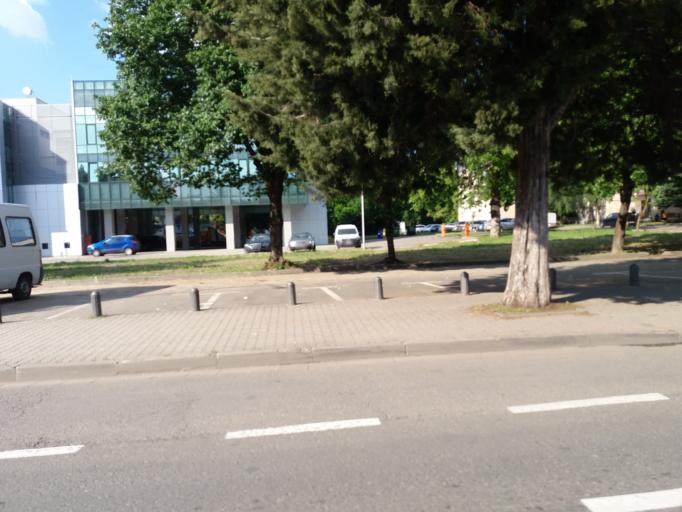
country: RO
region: Arad
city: Arad
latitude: 46.1841
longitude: 21.3203
